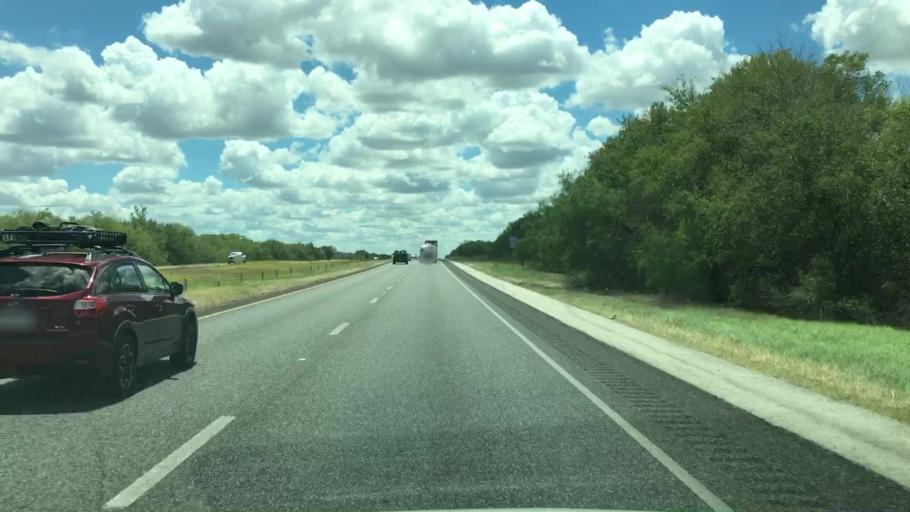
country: US
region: Texas
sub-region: Bexar County
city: Elmendorf
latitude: 29.1353
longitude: -98.4298
